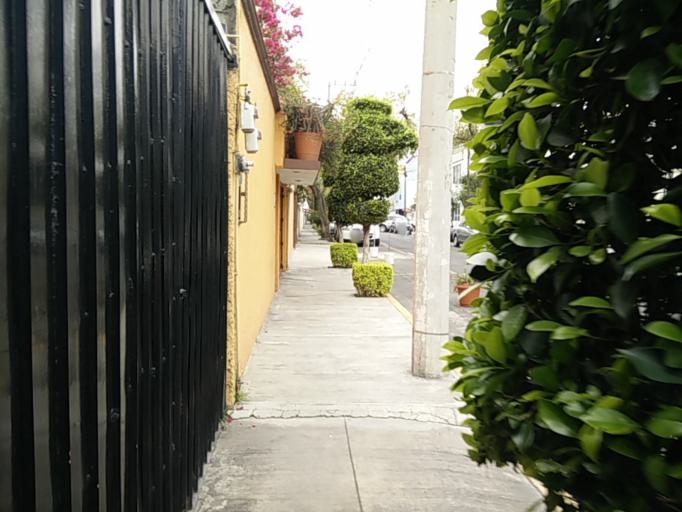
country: MX
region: Mexico
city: Colonia Lindavista
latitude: 19.4891
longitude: -99.1326
